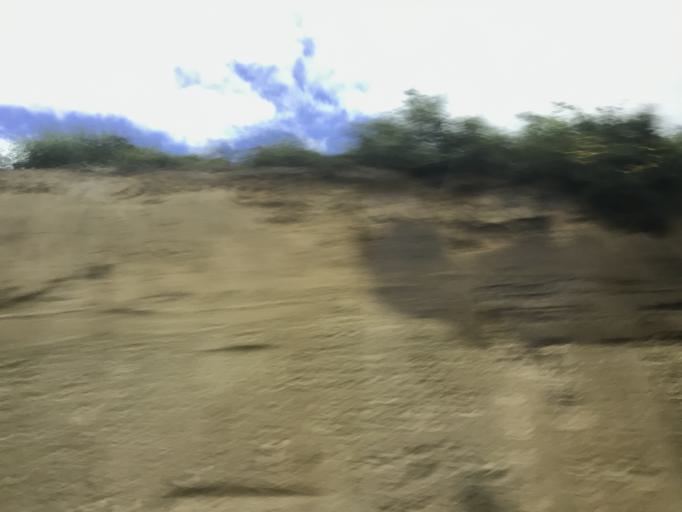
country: GT
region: Chimaltenango
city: El Tejar
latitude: 14.6312
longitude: -90.7919
